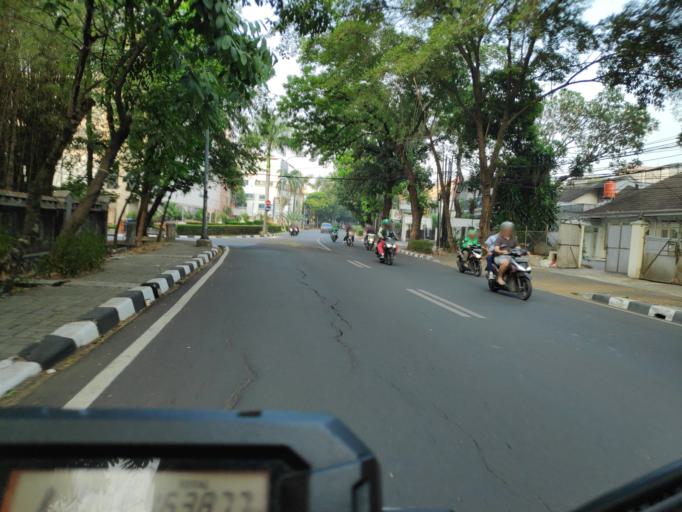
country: ID
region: Jakarta Raya
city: Jakarta
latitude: -6.2521
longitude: 106.8020
